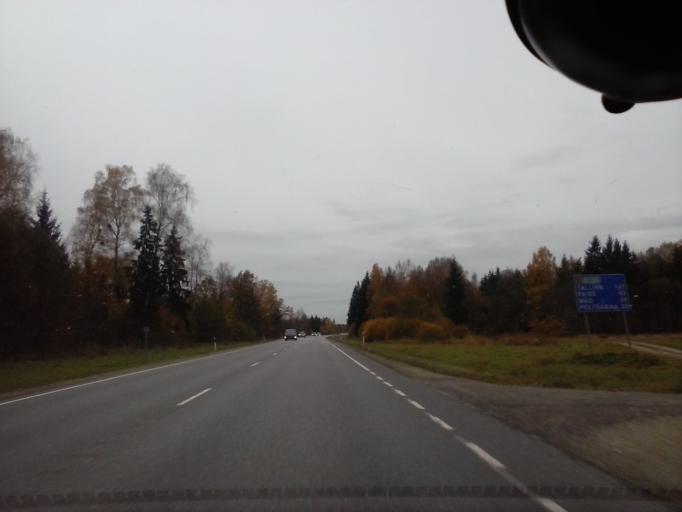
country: EE
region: Jogevamaa
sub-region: Jogeva linn
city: Jogeva
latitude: 58.5815
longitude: 26.2678
